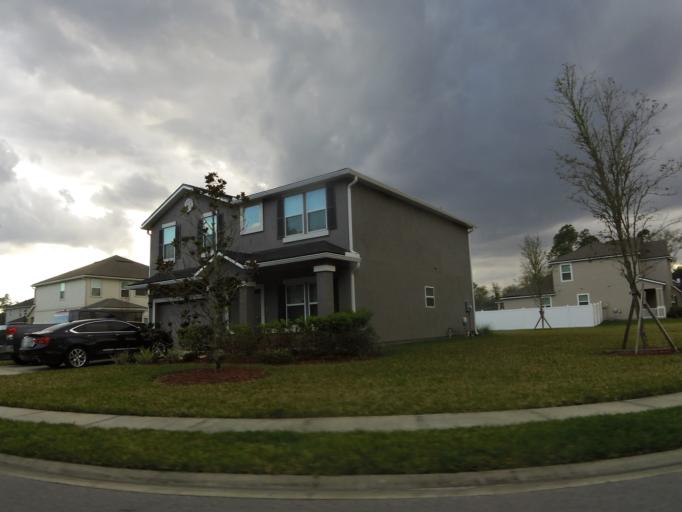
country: US
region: Florida
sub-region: Saint Johns County
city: Fruit Cove
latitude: 30.1726
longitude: -81.5659
